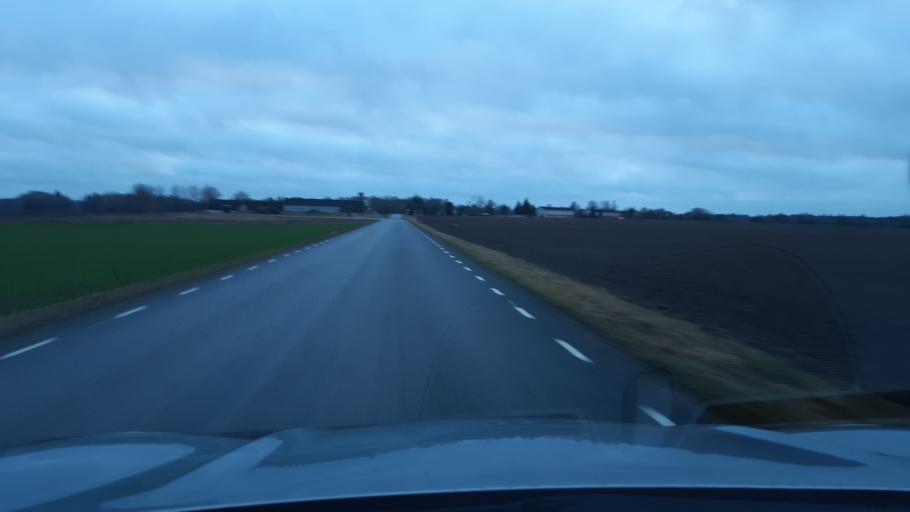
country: EE
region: Raplamaa
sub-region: Rapla vald
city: Rapla
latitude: 59.0468
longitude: 24.6782
